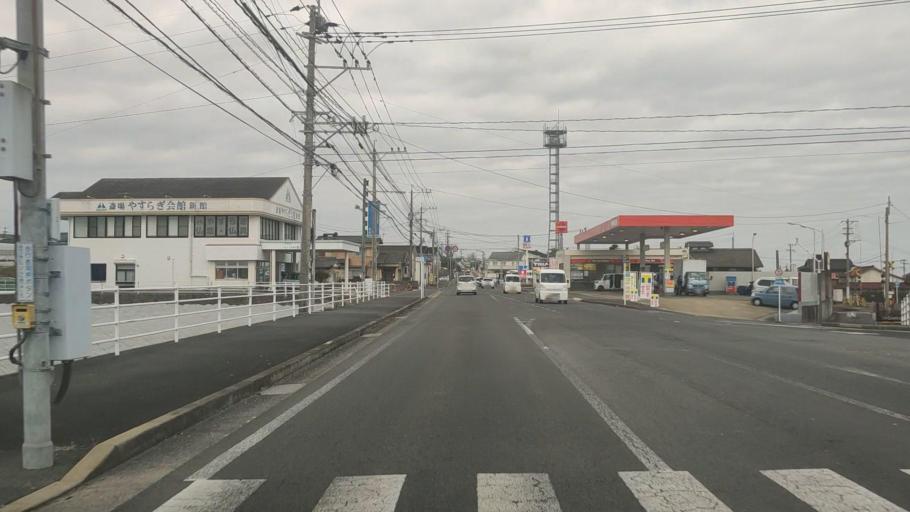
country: JP
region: Nagasaki
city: Shimabara
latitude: 32.8133
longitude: 130.3579
